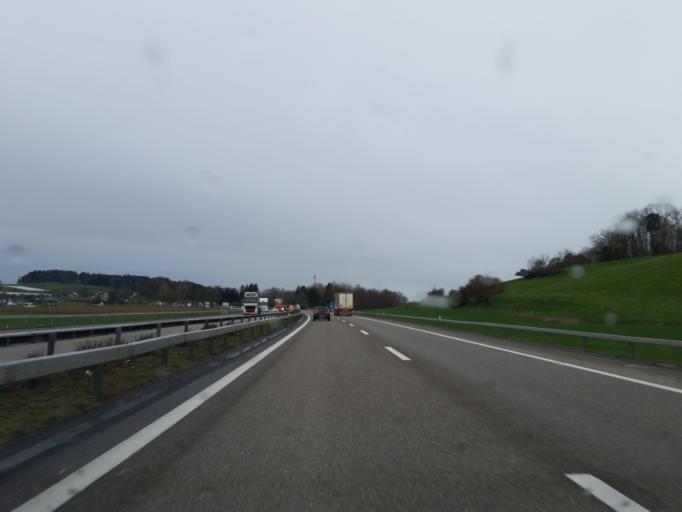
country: CH
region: Thurgau
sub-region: Frauenfeld District
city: Gachnang
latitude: 47.5544
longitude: 8.8429
